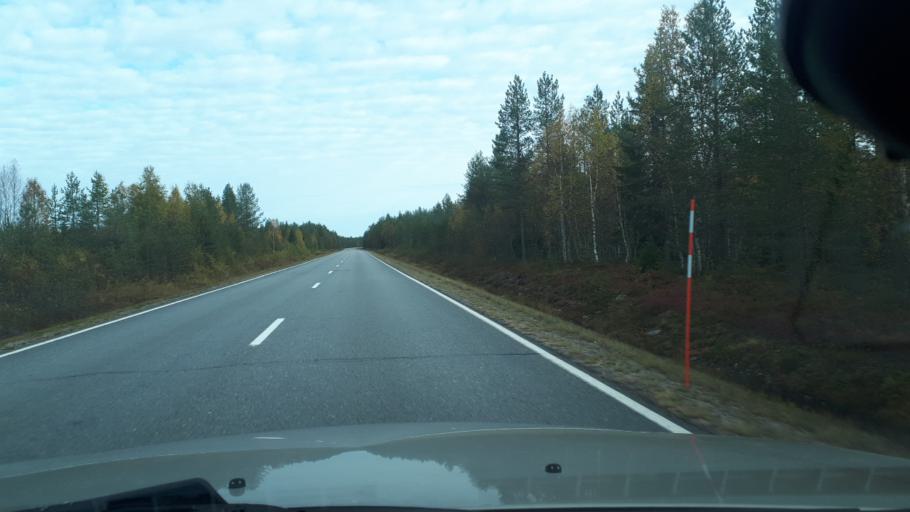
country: FI
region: Northern Ostrobothnia
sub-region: Oulu
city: Yli-Ii
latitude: 65.9046
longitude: 25.7365
